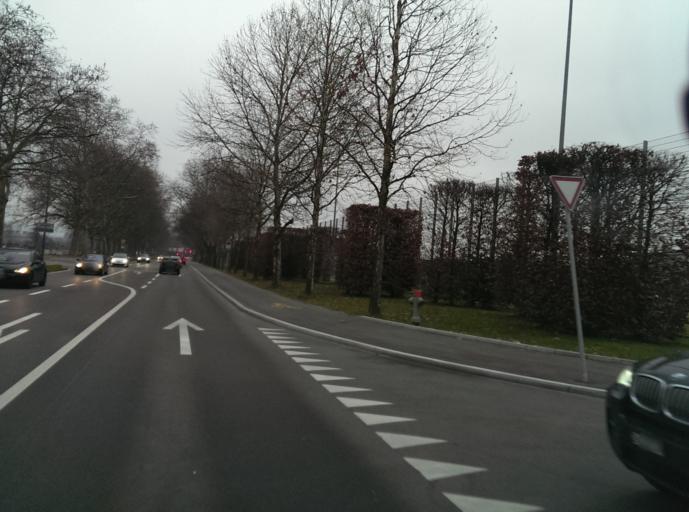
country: CH
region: Zurich
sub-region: Bezirk Dietikon
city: Oberengstringen / Zentrum
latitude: 47.3996
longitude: 8.4679
